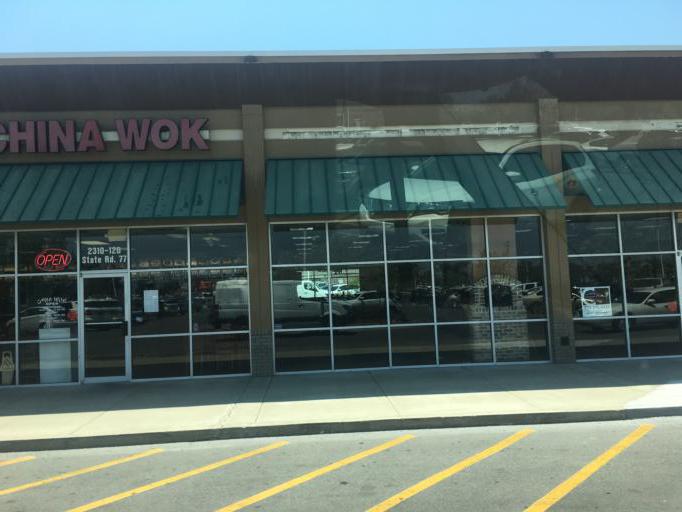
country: US
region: Florida
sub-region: Bay County
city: Lynn Haven
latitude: 30.2224
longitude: -85.6512
